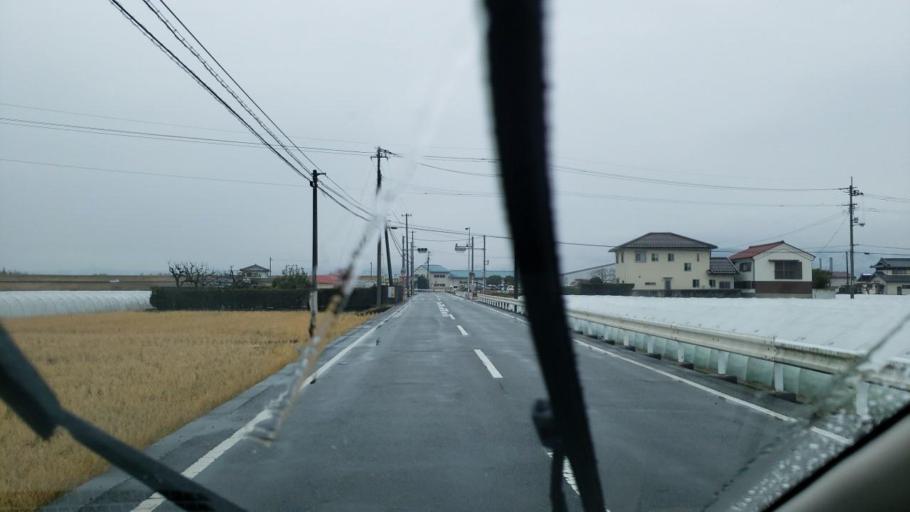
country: JP
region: Tokushima
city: Ishii
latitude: 34.1003
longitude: 134.4071
